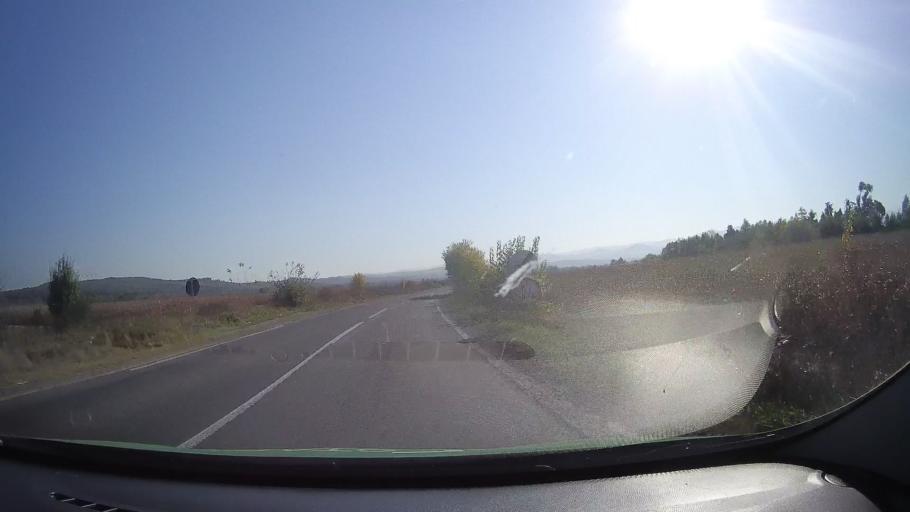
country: RO
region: Timis
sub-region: Comuna Margina
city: Margina
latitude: 45.8564
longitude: 22.2747
